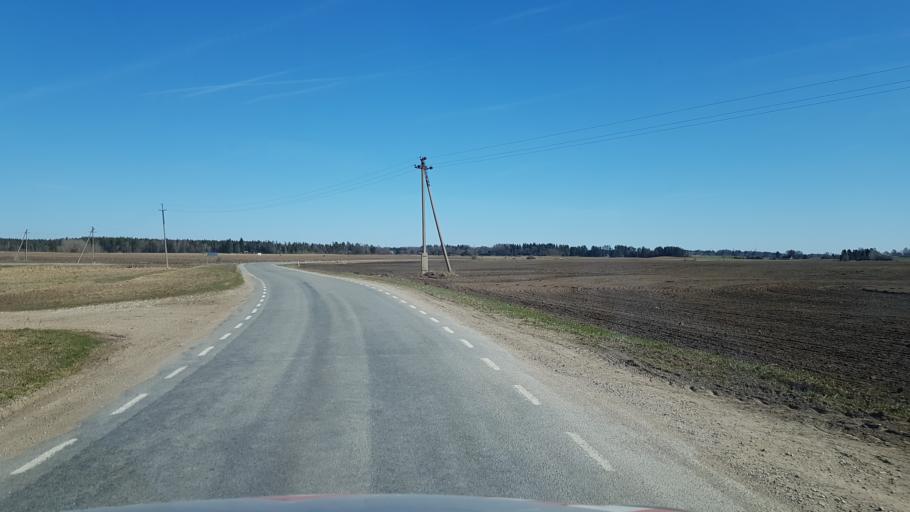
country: EE
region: Laeaene-Virumaa
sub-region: Someru vald
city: Someru
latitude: 59.3396
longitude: 26.5139
